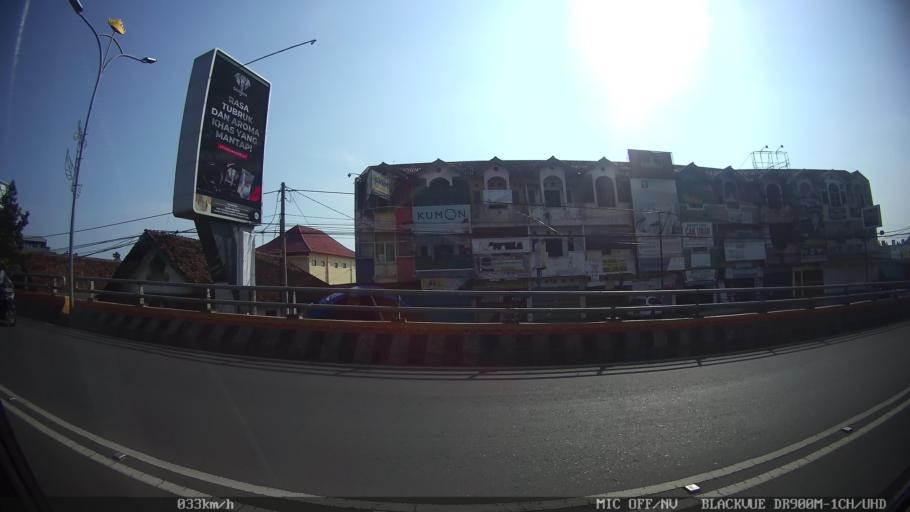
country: ID
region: Lampung
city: Kedaton
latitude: -5.3838
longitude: 105.2603
